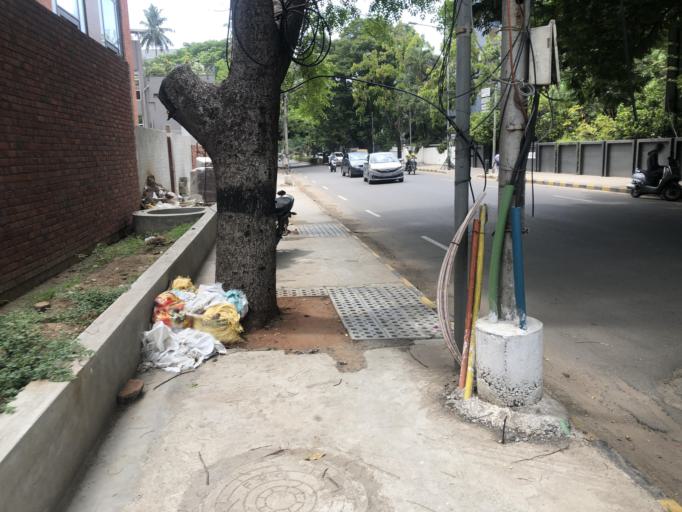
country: IN
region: Tamil Nadu
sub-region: Chennai
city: Gandhi Nagar
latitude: 13.0287
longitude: 80.2501
